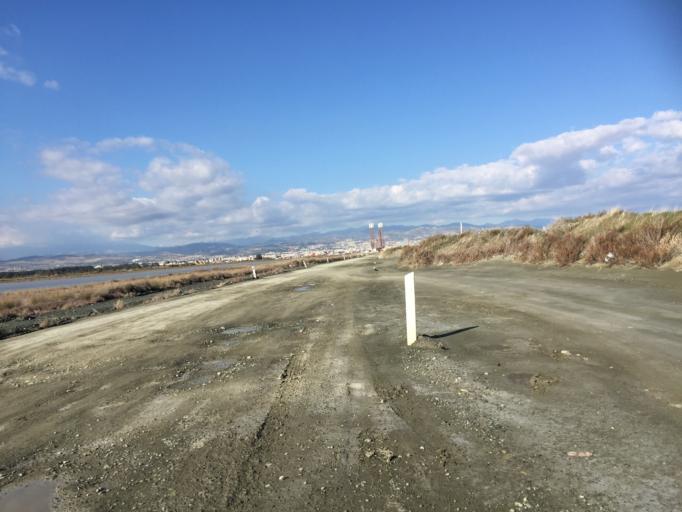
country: CY
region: Limassol
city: Limassol
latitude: 34.6271
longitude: 33.0062
